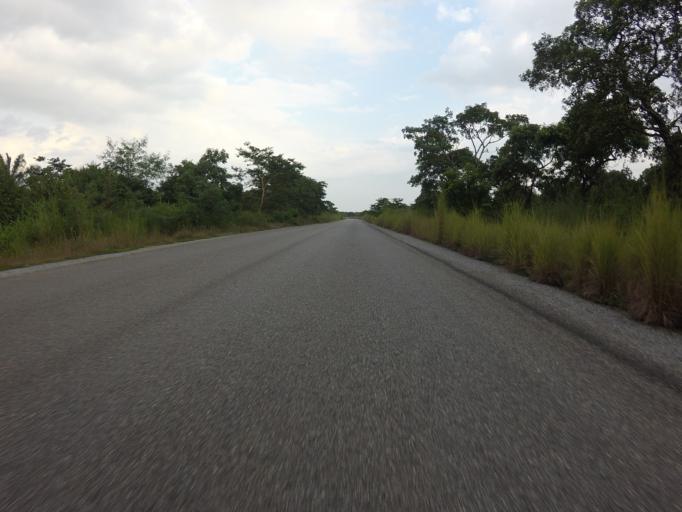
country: GH
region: Volta
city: Ho
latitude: 6.4346
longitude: 0.5058
